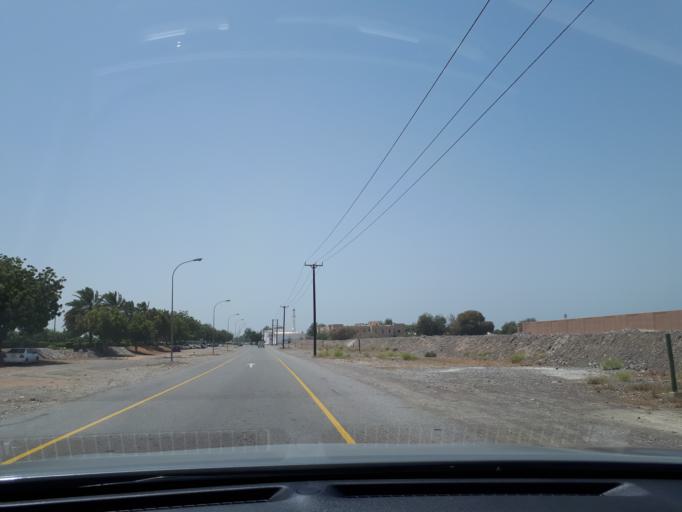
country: OM
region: Muhafazat Masqat
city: As Sib al Jadidah
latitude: 23.6919
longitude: 58.0774
